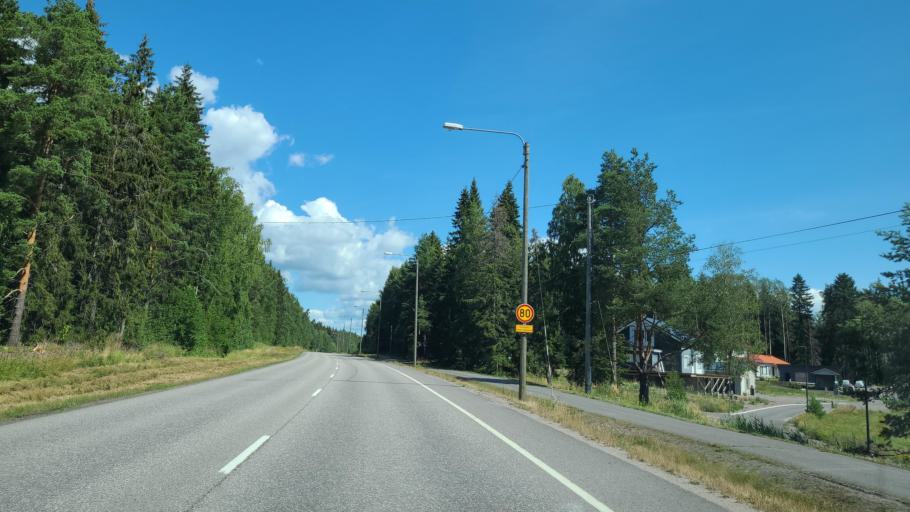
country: FI
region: Uusimaa
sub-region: Porvoo
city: Porvoo
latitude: 60.3522
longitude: 25.5982
